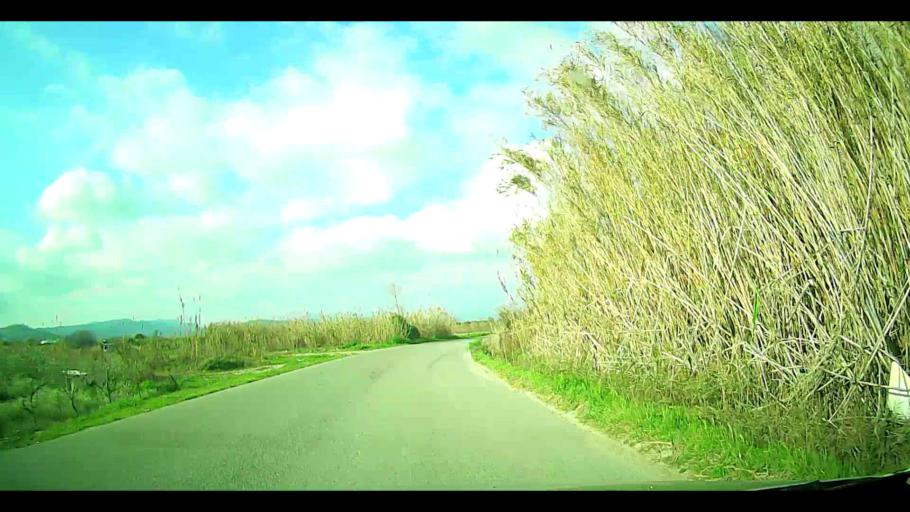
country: IT
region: Calabria
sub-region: Provincia di Crotone
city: Rocca di Neto
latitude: 39.1799
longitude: 17.0349
